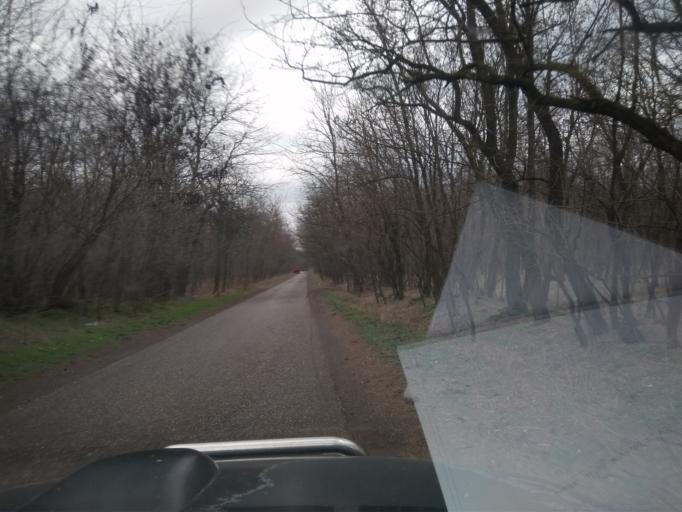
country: HU
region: Szabolcs-Szatmar-Bereg
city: Nyirpazony
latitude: 48.0242
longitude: 21.7993
